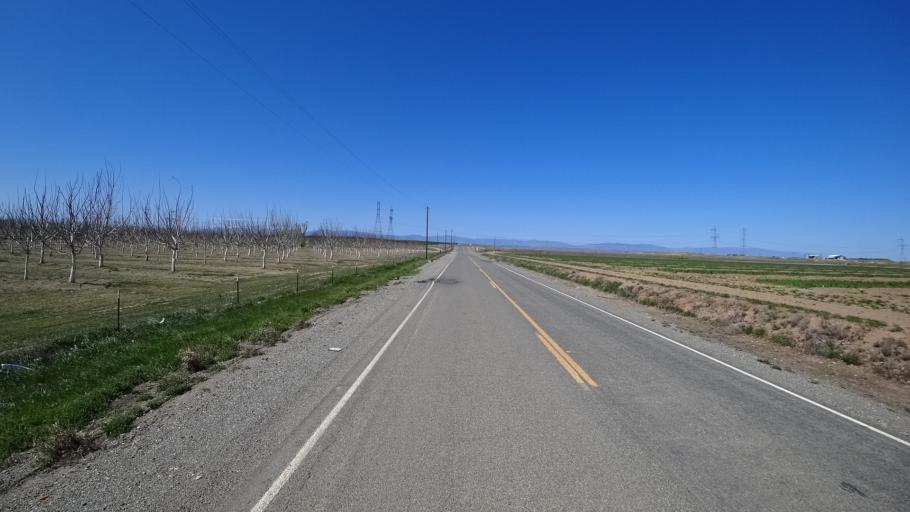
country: US
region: California
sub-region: Glenn County
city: Willows
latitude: 39.6248
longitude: -122.2693
